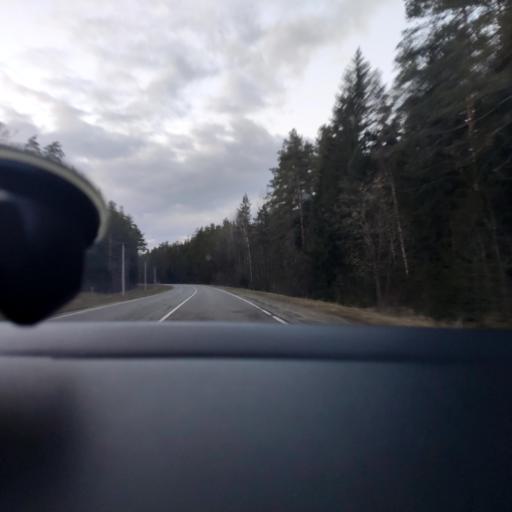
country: RU
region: Moskovskaya
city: Shaturtorf
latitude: 55.4414
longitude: 39.4339
